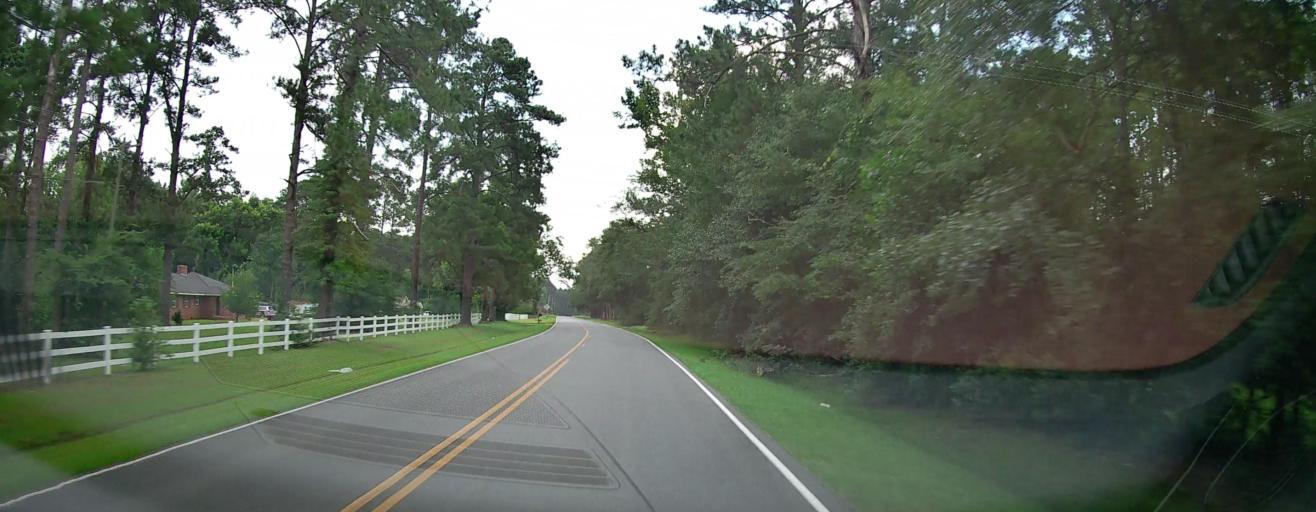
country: US
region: Georgia
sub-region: Laurens County
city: Dublin
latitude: 32.5791
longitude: -82.9042
